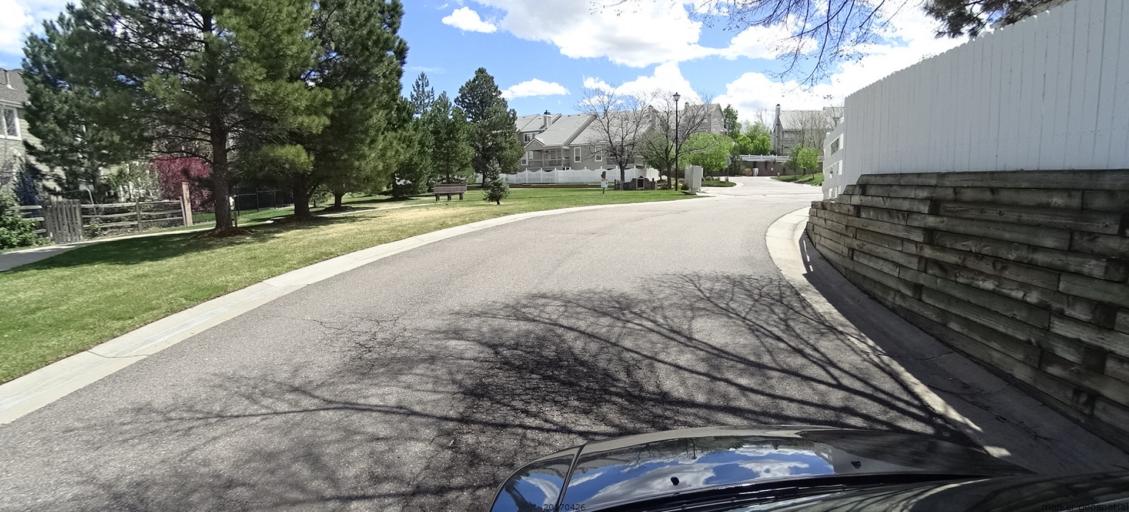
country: US
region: Colorado
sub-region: Douglas County
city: Carriage Club
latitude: 39.5382
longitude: -104.8930
